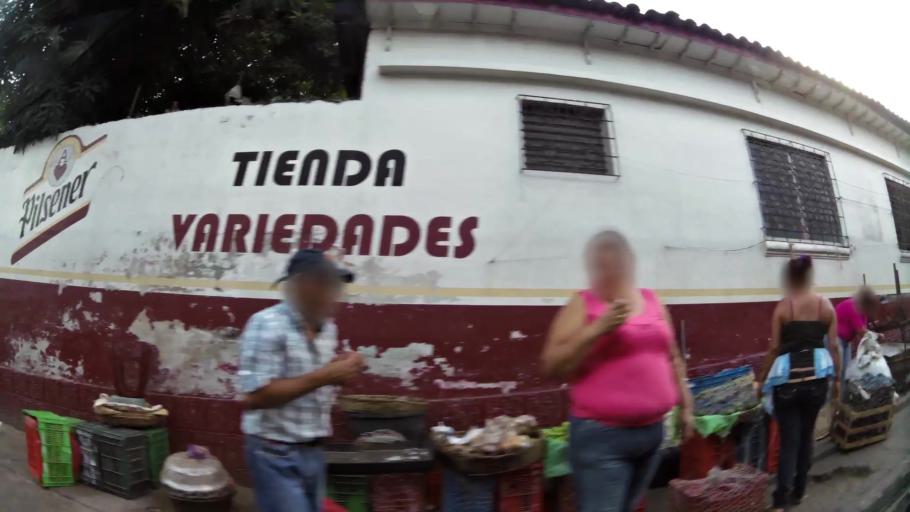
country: SV
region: San Vicente
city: San Vicente
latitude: 13.6426
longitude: -88.7871
